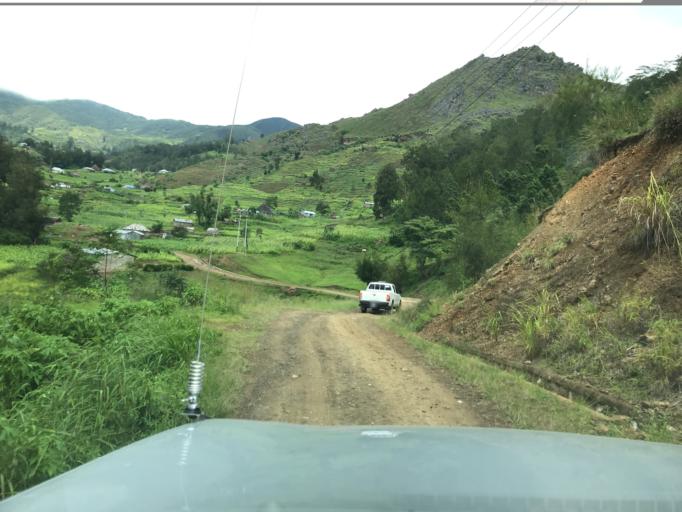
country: TL
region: Aileu
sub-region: Aileu Villa
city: Aileu
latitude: -8.8589
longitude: 125.5743
